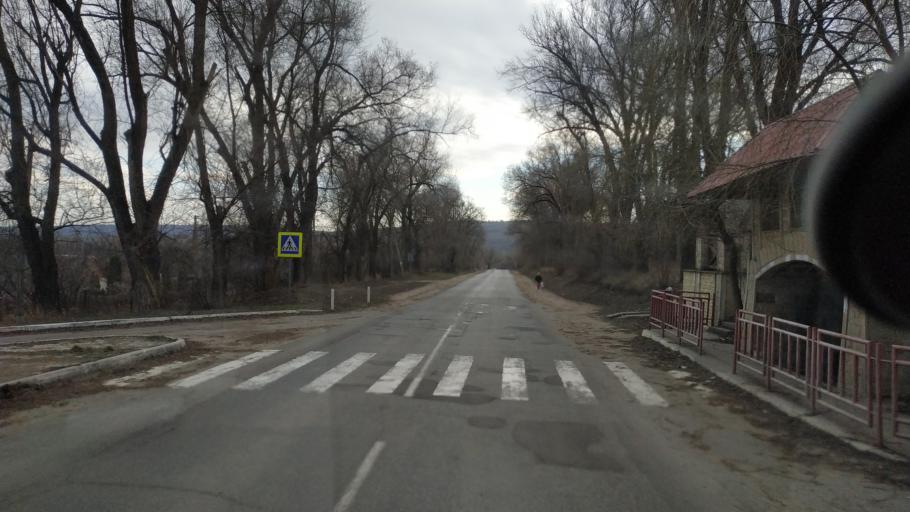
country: MD
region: Chisinau
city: Vadul lui Voda
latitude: 47.1214
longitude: 29.0638
